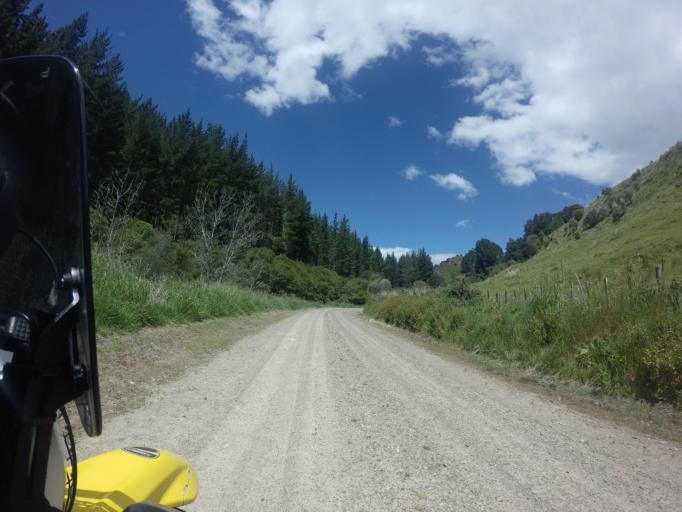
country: NZ
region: Hawke's Bay
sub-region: Wairoa District
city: Wairoa
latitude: -38.9671
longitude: 177.6690
